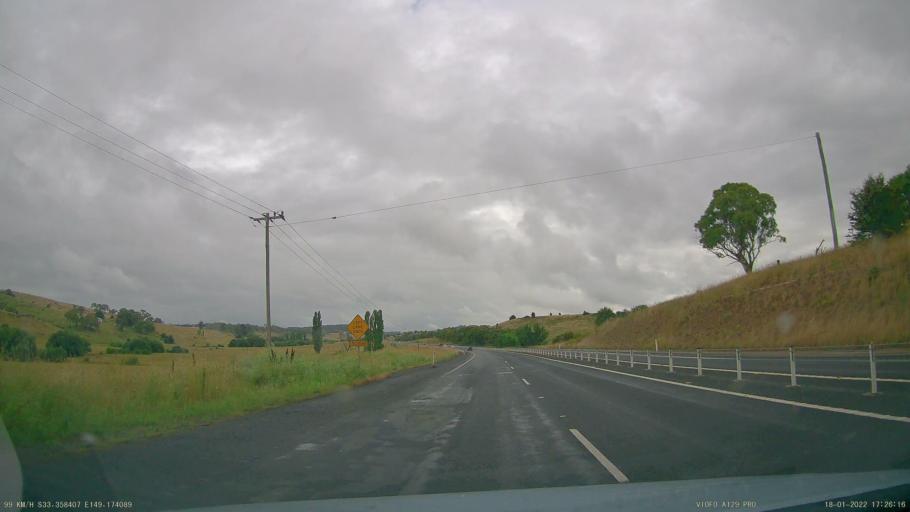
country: AU
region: New South Wales
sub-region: Blayney
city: Millthorpe
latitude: -33.3587
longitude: 149.1742
